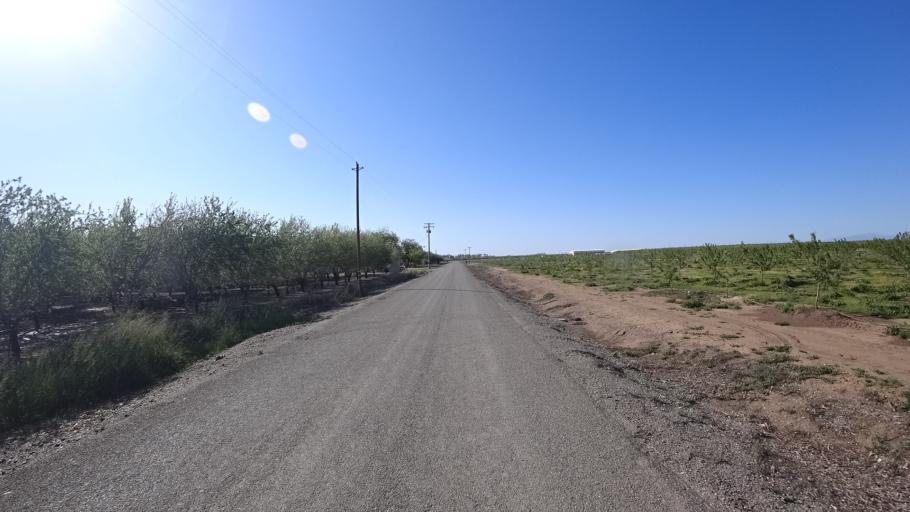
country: US
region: California
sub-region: Glenn County
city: Hamilton City
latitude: 39.7709
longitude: -122.0477
